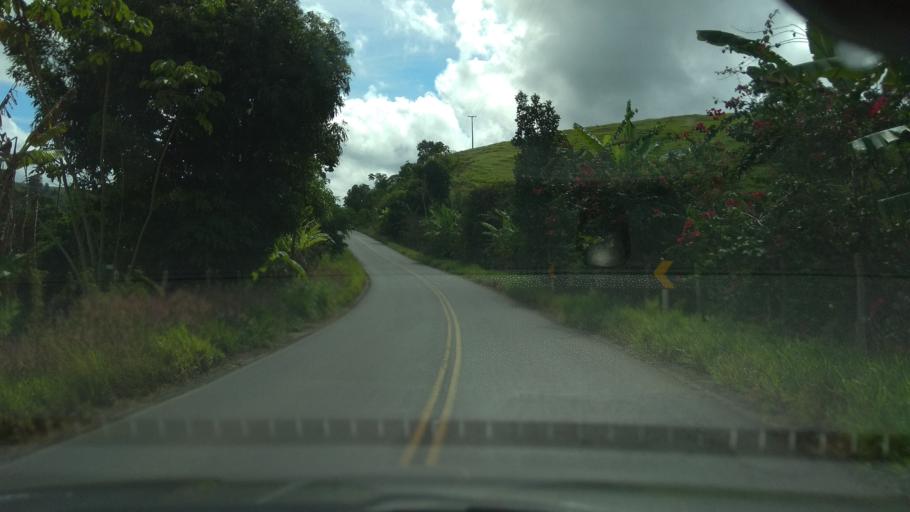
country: BR
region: Bahia
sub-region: Mutuipe
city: Mutuipe
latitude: -13.1943
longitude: -39.4588
